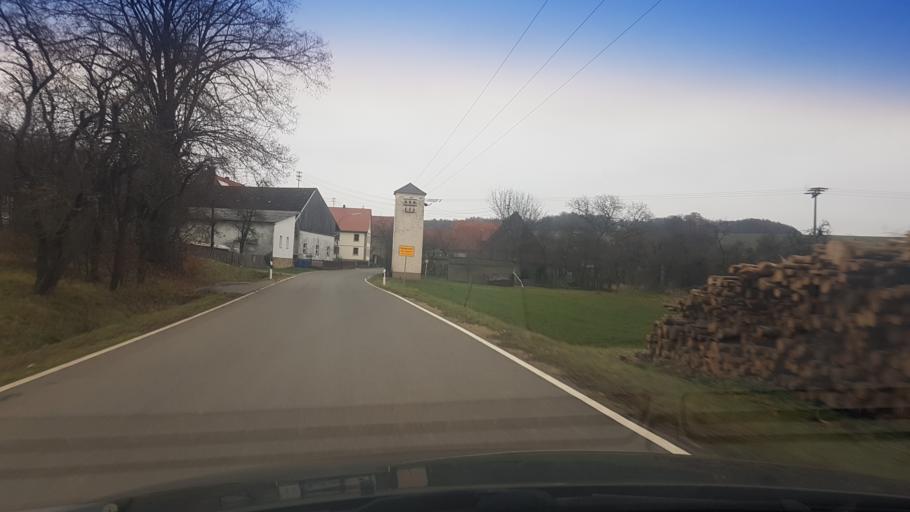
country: DE
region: Bavaria
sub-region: Upper Franconia
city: Zapfendorf
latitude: 50.0130
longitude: 10.9885
